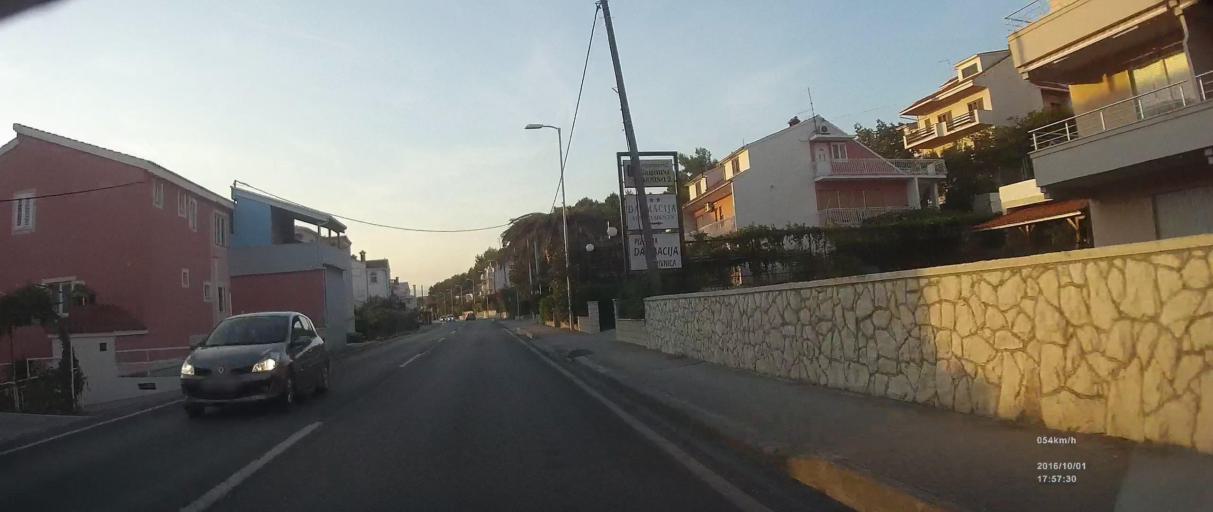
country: HR
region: Splitsko-Dalmatinska
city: Srinjine
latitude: 43.4703
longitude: 16.5743
